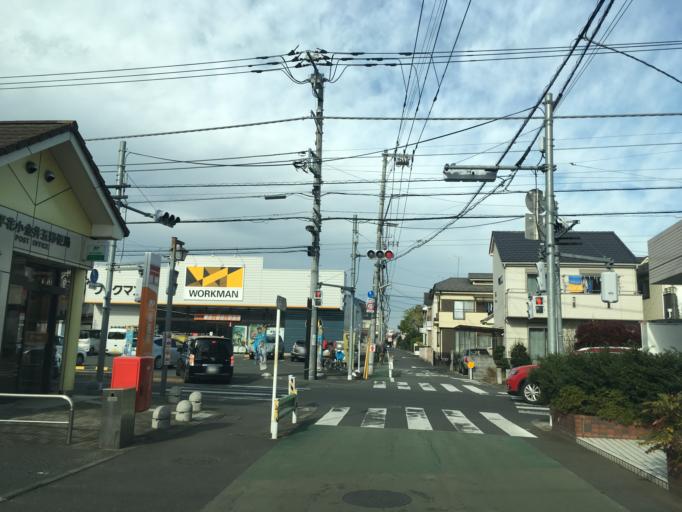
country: JP
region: Tokyo
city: Tanashicho
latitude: 35.7359
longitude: 139.5066
